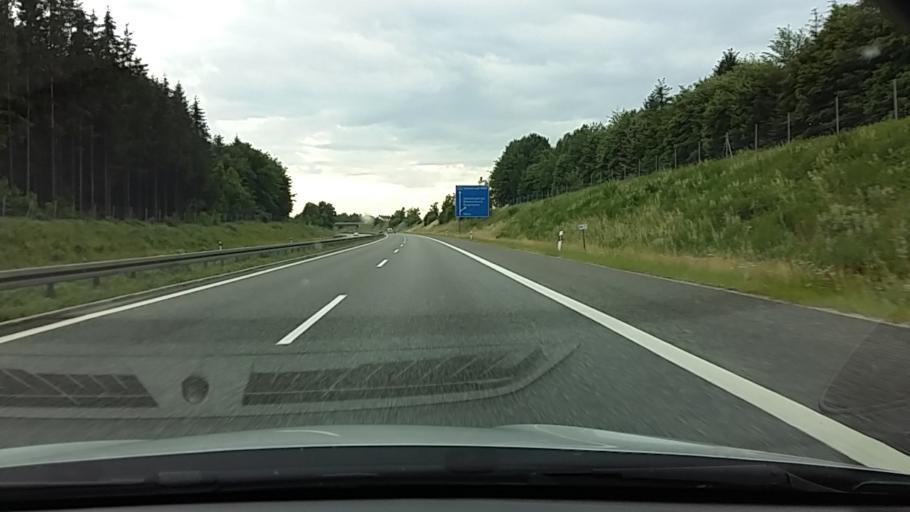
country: DE
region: Bavaria
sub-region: Upper Palatinate
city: Vohenstrauss
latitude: 49.6190
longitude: 12.3651
